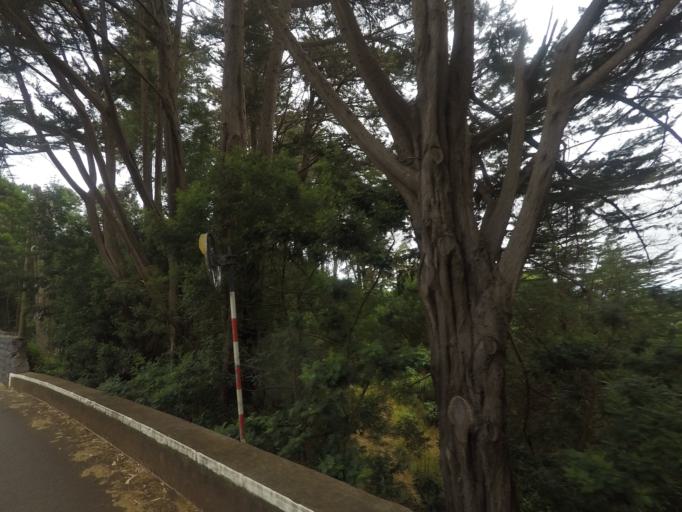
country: PT
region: Madeira
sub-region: Funchal
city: Nossa Senhora do Monte
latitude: 32.6684
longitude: -16.8791
